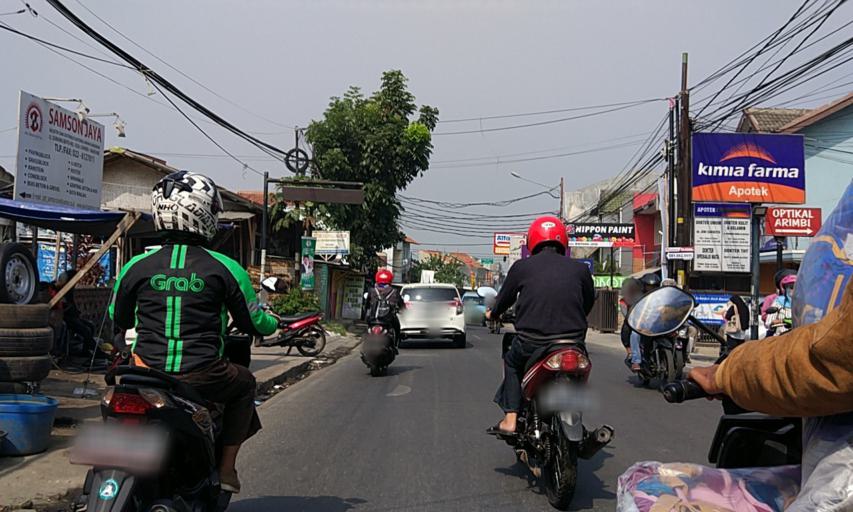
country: ID
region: West Java
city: Cimahi
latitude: -6.8905
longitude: 107.5637
